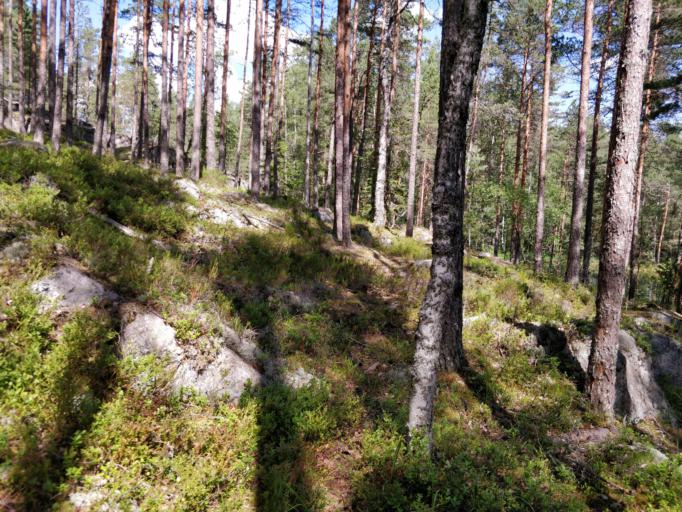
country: FI
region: Uusimaa
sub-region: Helsinki
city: Vihti
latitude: 60.3115
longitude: 24.4771
